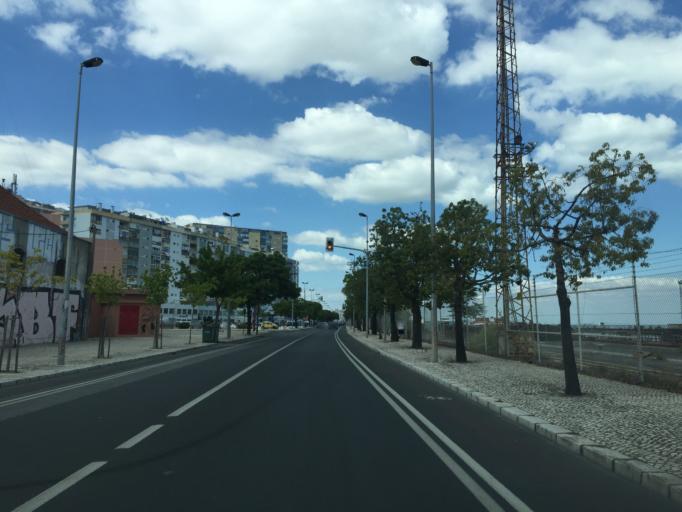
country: PT
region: Setubal
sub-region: Almada
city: Cacilhas
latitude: 38.6815
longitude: -9.1489
